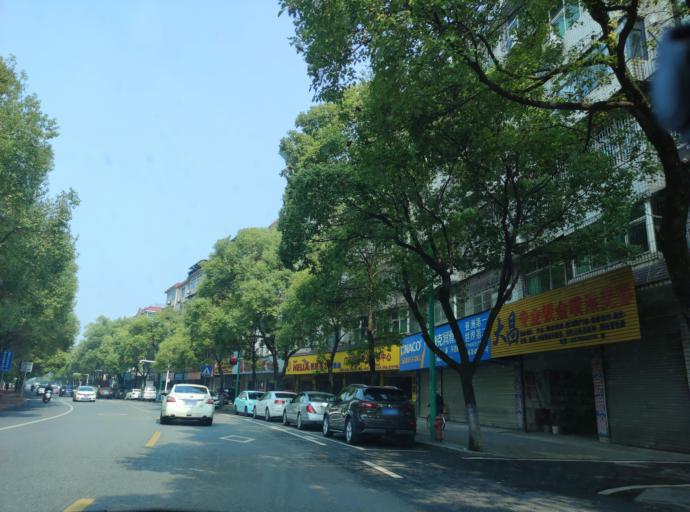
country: CN
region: Jiangxi Sheng
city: Pingxiang
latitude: 27.6417
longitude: 113.8562
